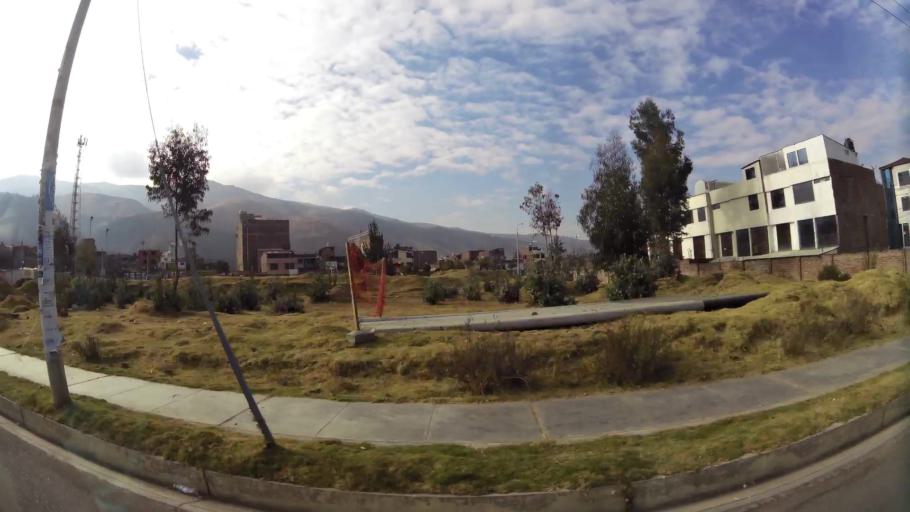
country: PE
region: Junin
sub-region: Provincia de Huancayo
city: Huancayo
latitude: -12.0415
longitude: -75.1947
